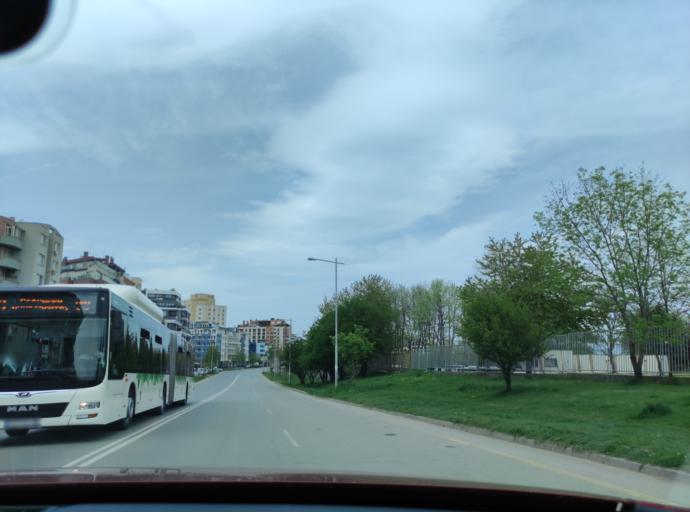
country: BG
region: Sofia-Capital
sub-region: Stolichna Obshtina
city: Sofia
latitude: 42.6450
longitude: 23.3452
